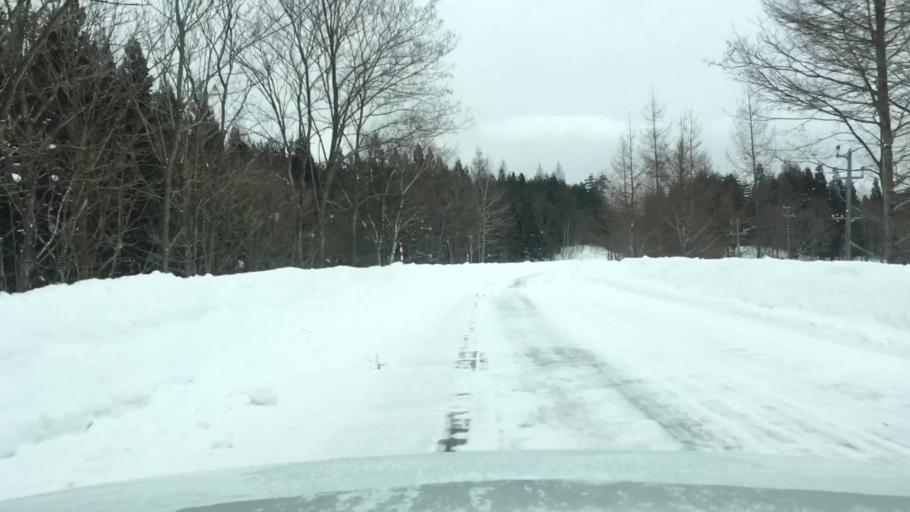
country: JP
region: Akita
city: Hanawa
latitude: 39.9886
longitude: 140.9978
